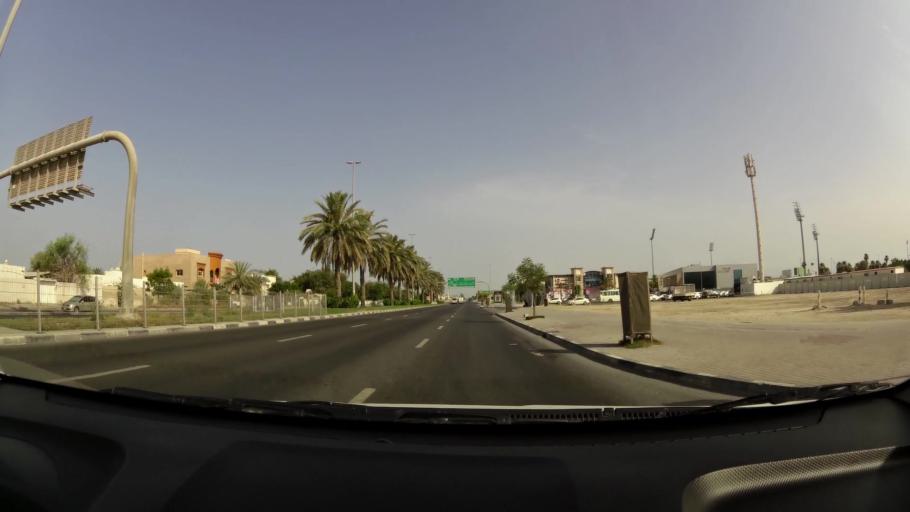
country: AE
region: Ash Shariqah
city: Sharjah
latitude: 25.2874
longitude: 55.3489
